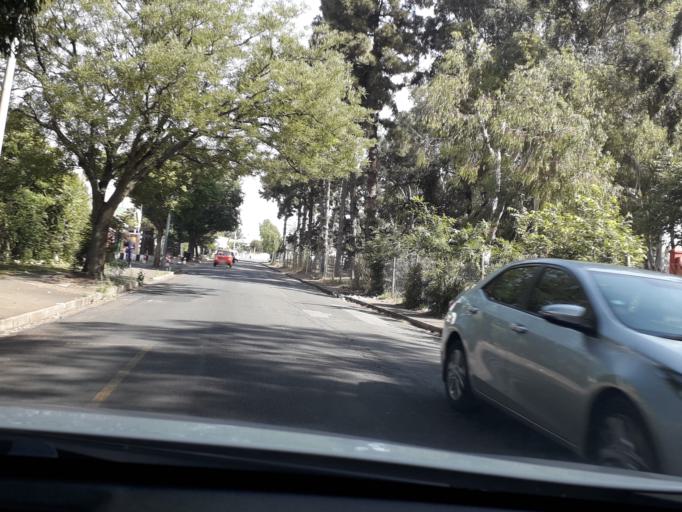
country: ZA
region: Gauteng
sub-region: City of Johannesburg Metropolitan Municipality
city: Johannesburg
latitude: -26.1957
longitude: 28.0062
